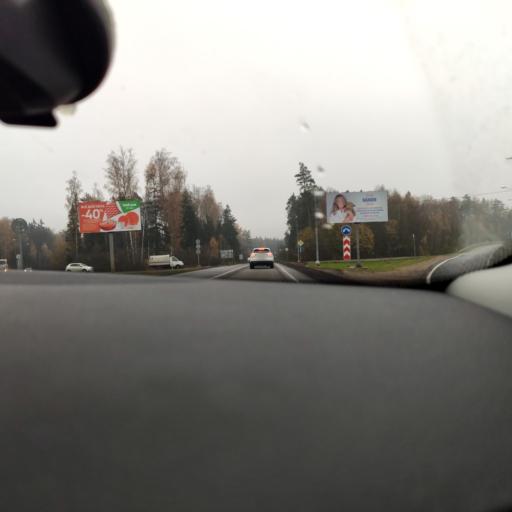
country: RU
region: Moskovskaya
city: Petrovo-Dal'neye
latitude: 55.7845
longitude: 37.1591
